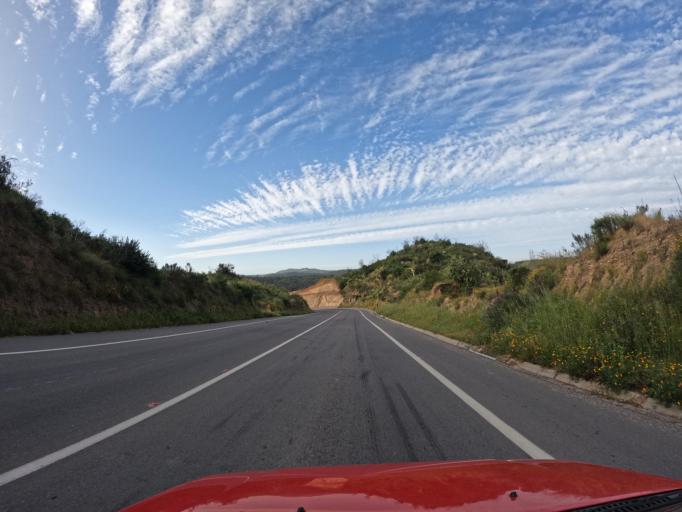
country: CL
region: Valparaiso
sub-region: San Antonio Province
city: San Antonio
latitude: -34.0440
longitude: -71.5928
